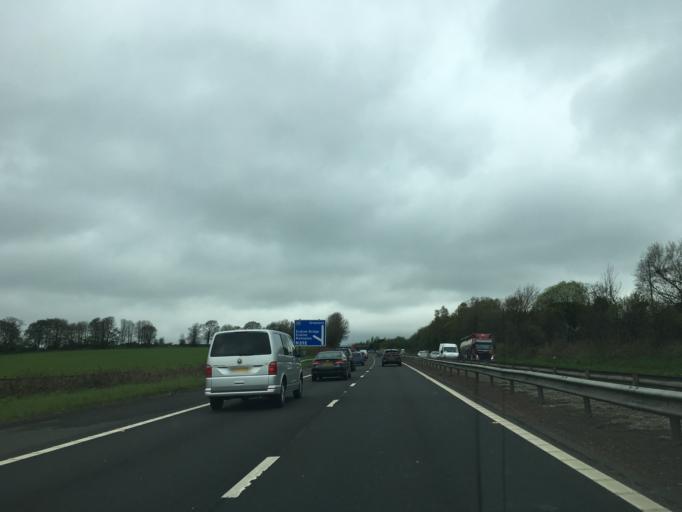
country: GB
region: Scotland
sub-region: Renfrewshire
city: Bishopton
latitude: 55.8957
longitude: -4.4823
